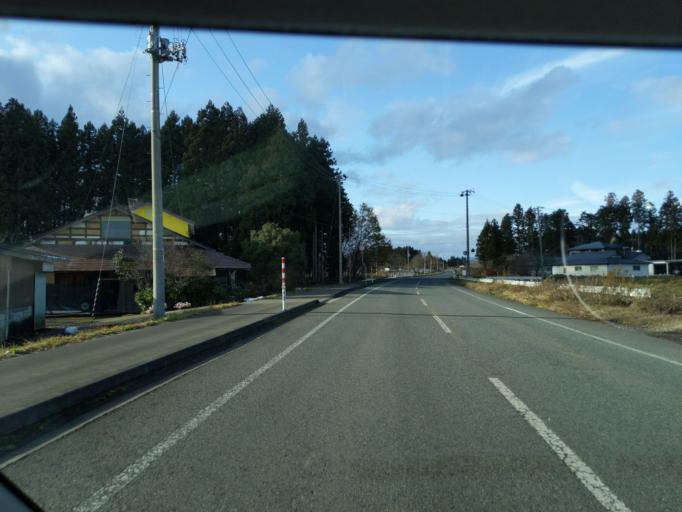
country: JP
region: Iwate
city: Mizusawa
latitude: 39.1913
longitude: 141.0735
